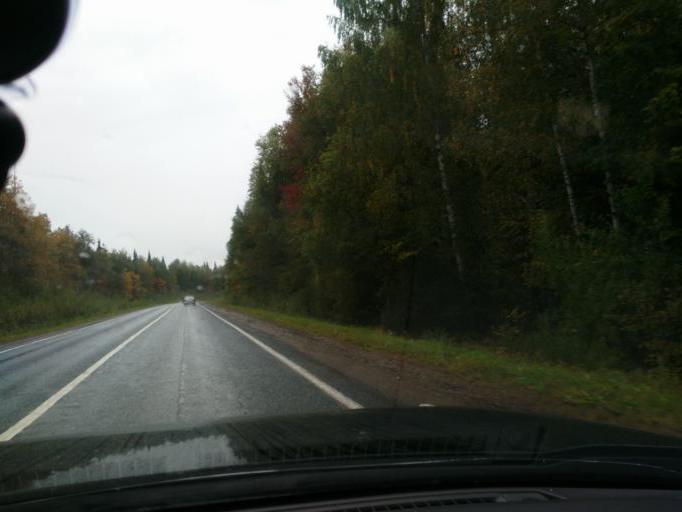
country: RU
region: Perm
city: Yugo-Kamskiy
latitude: 57.5964
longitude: 55.6576
